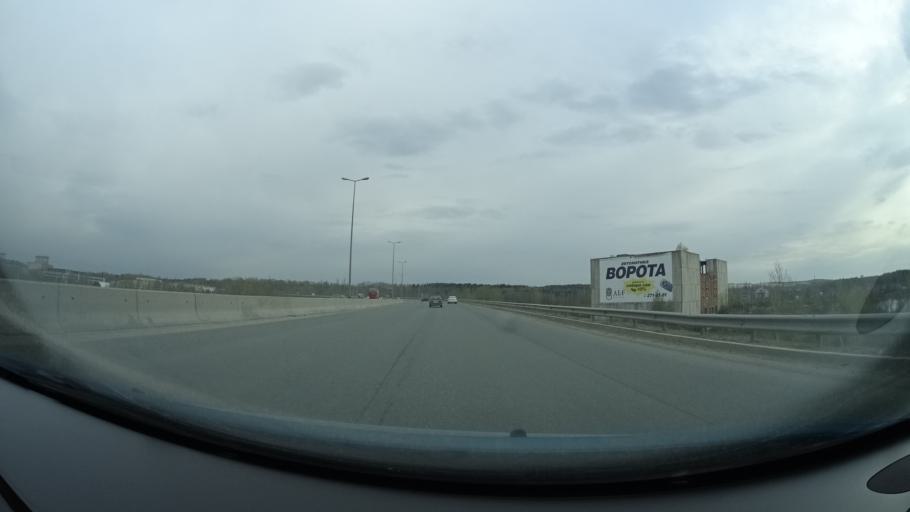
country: RU
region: Perm
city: Kondratovo
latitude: 58.0302
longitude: 56.0561
